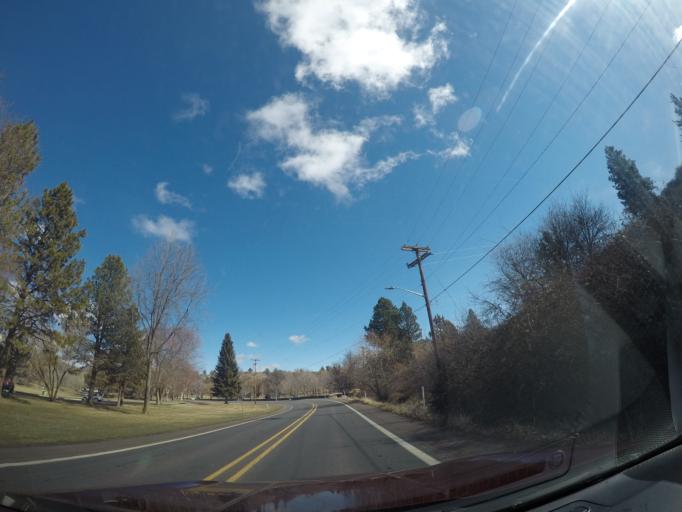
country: US
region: Oregon
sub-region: Klamath County
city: Klamath Falls
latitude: 42.2336
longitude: -121.8111
